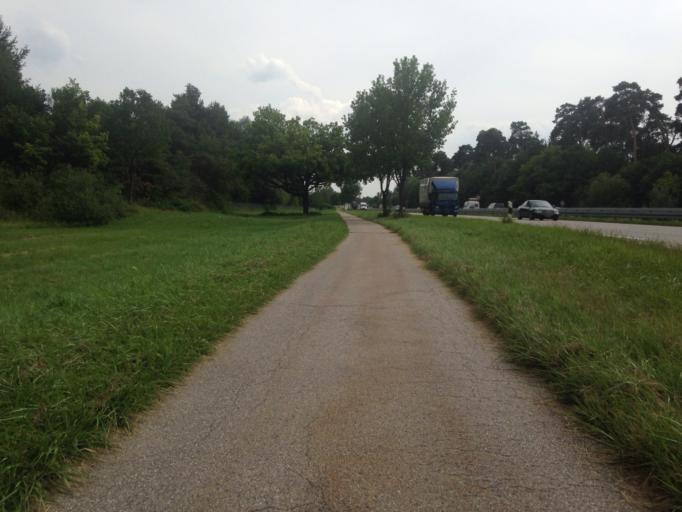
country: DE
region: Bavaria
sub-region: Upper Bavaria
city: Oberschleissheim
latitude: 48.2348
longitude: 11.5993
